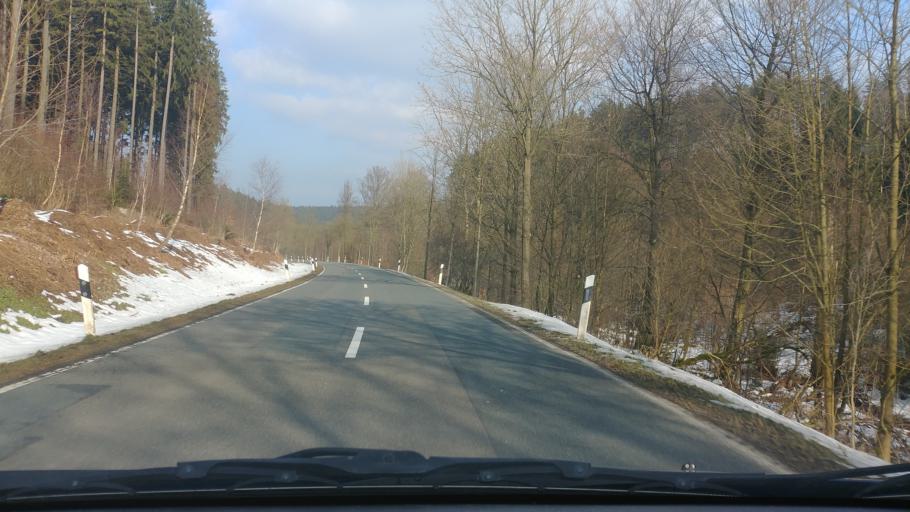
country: DE
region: Lower Saxony
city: Uslar
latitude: 51.7264
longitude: 9.6269
